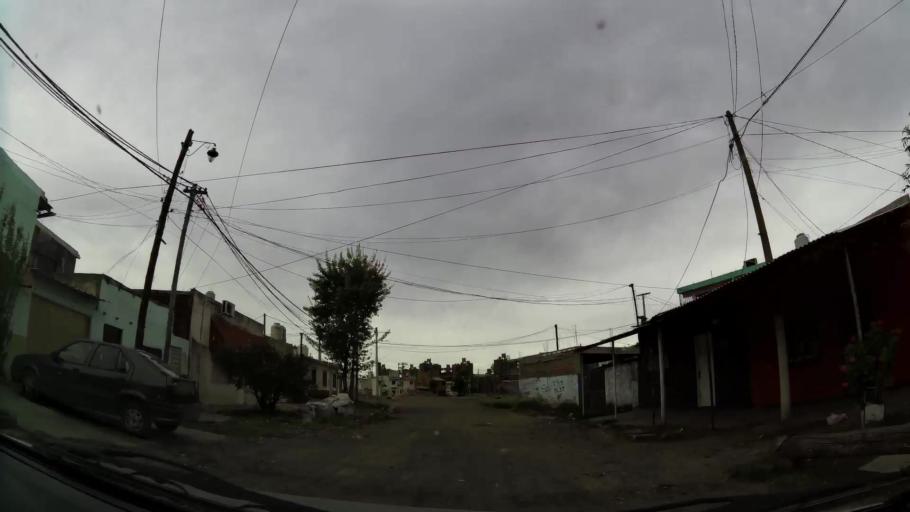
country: AR
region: Buenos Aires
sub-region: Partido de Avellaneda
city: Avellaneda
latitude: -34.6532
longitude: -58.3560
